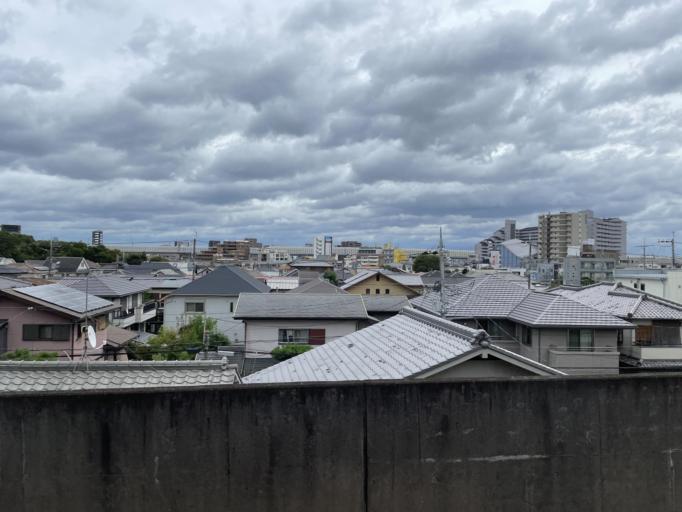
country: JP
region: Hyogo
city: Kawanishi
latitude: 34.8294
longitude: 135.4169
